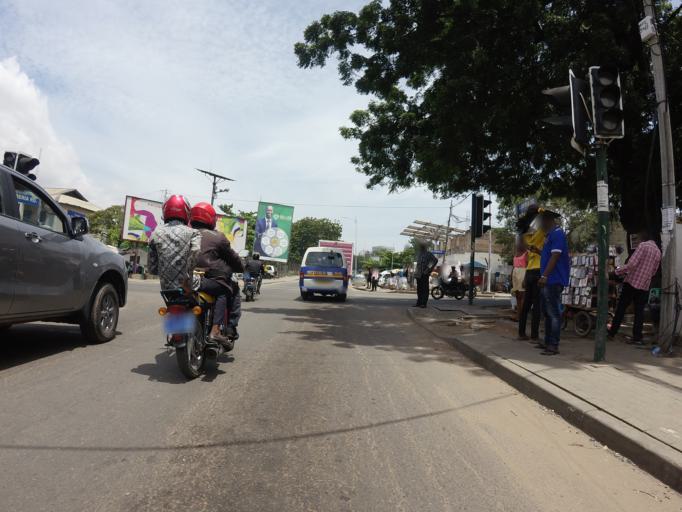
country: GH
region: Greater Accra
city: Accra
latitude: 5.5555
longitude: -0.2091
